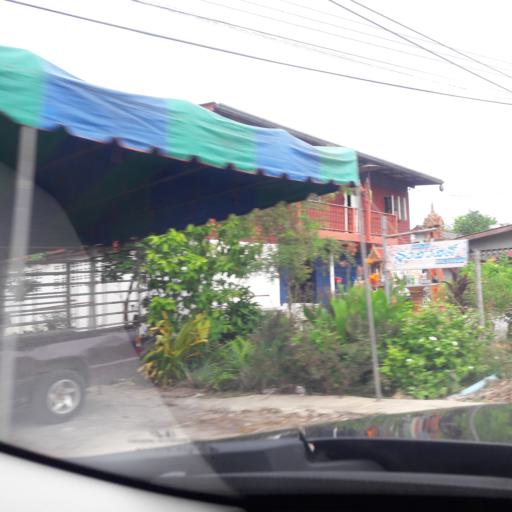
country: TH
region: Ratchaburi
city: Damnoen Saduak
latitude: 13.5622
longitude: 99.9459
